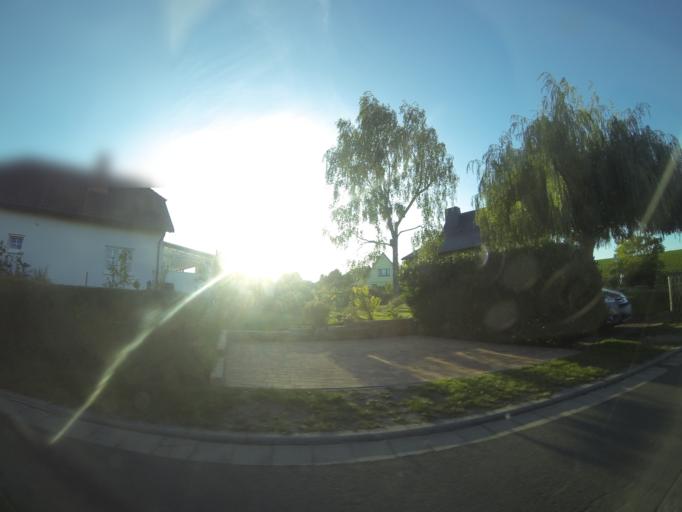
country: DE
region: Thuringia
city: Schmolln
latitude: 50.8916
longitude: 12.3715
